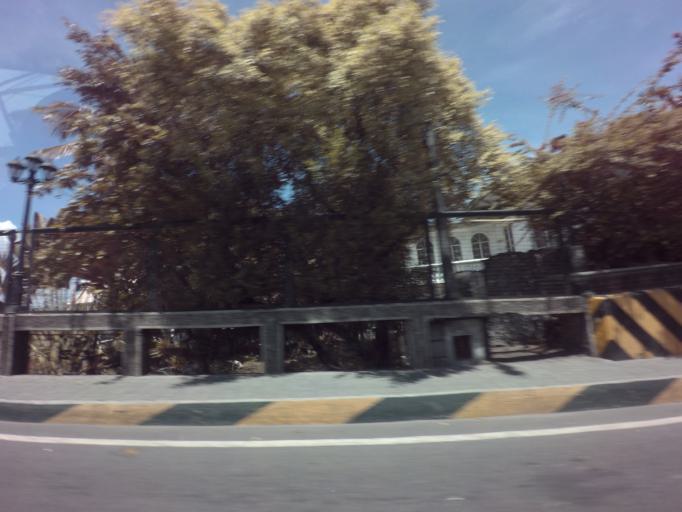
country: PH
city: Sambayanihan People's Village
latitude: 14.5018
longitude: 120.9927
